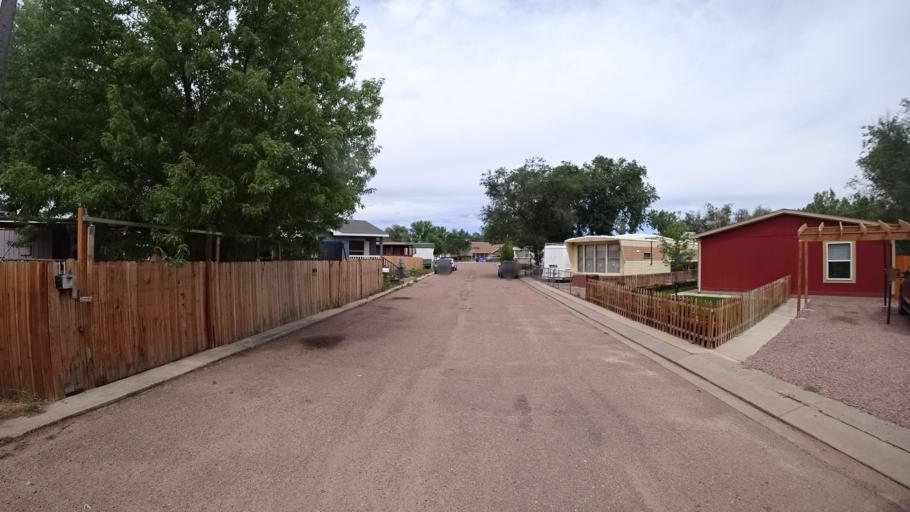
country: US
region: Colorado
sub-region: El Paso County
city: Fountain
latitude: 38.6771
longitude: -104.7061
